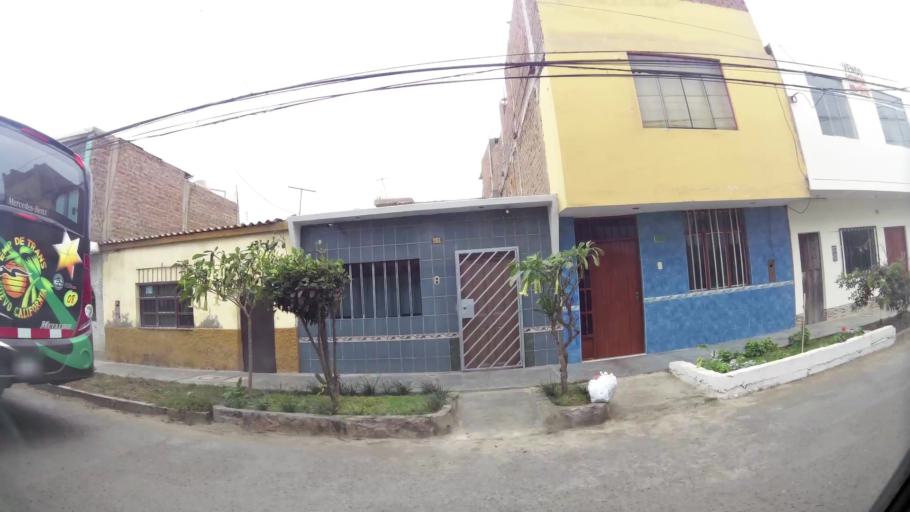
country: PE
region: La Libertad
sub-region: Provincia de Trujillo
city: Buenos Aires
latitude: -8.1418
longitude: -79.0564
